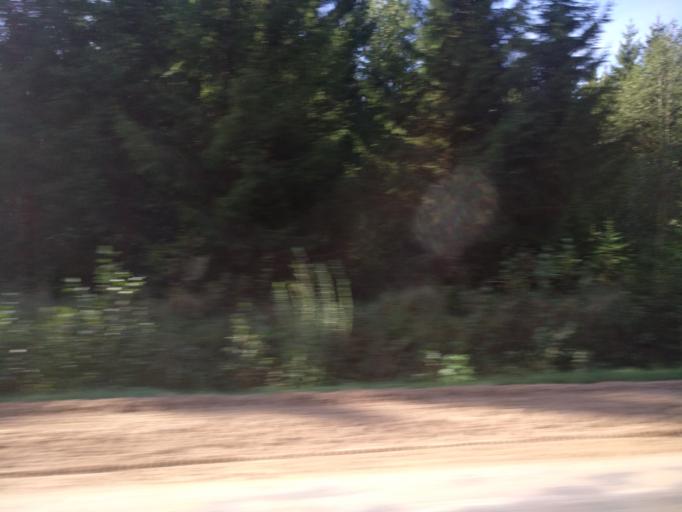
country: BY
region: Vitebsk
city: Mosar
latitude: 55.1431
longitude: 27.1842
